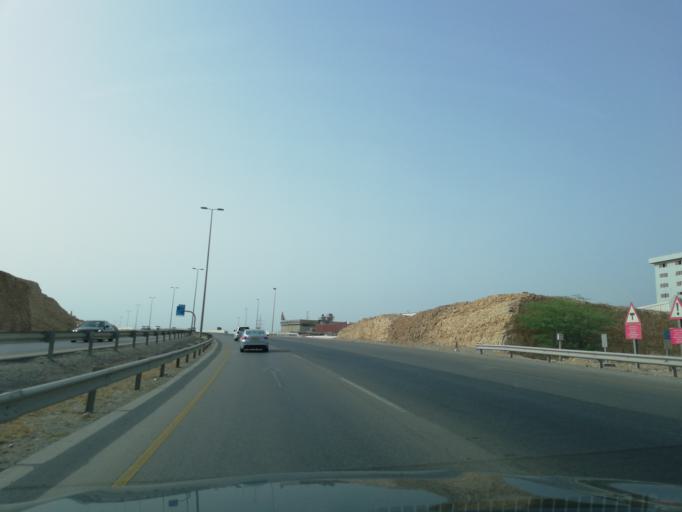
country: OM
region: Muhafazat Masqat
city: As Sib al Jadidah
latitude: 23.5540
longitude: 58.1945
